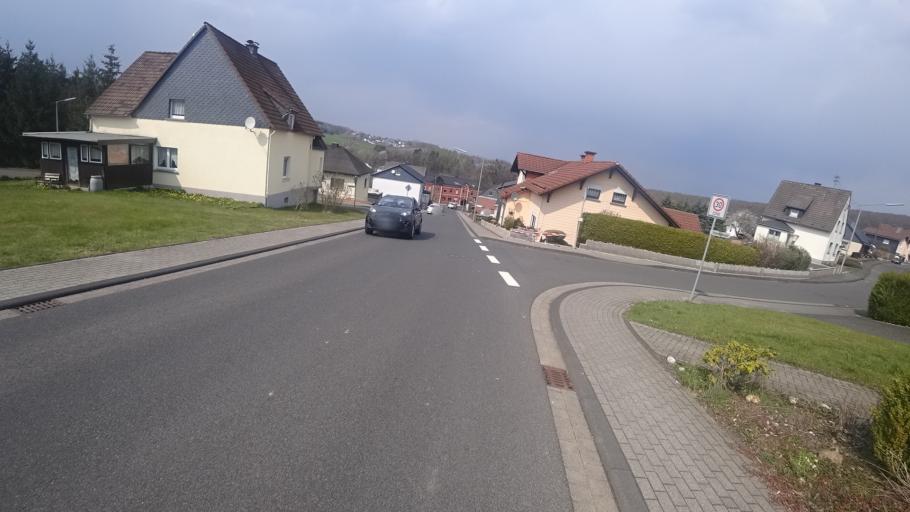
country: DE
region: Rheinland-Pfalz
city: Elben
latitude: 50.7306
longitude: 7.8270
